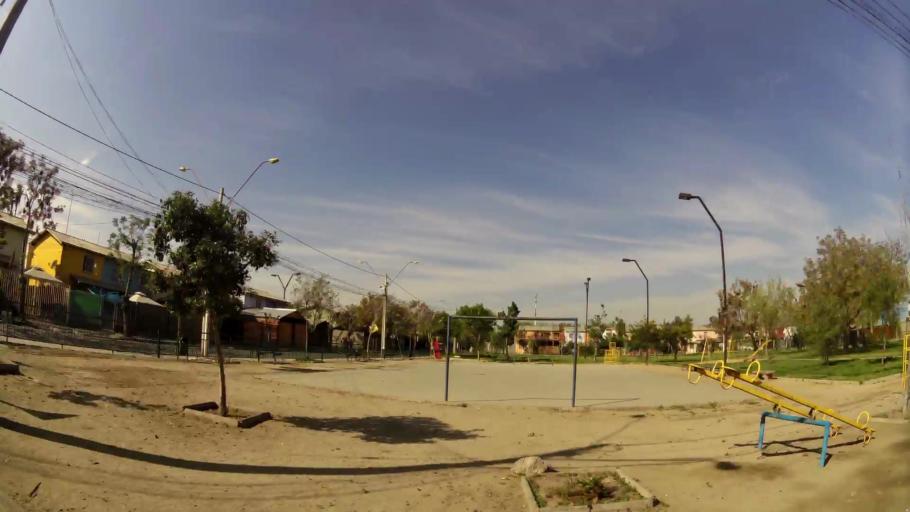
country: CL
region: Santiago Metropolitan
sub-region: Provincia de Santiago
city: La Pintana
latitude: -33.5638
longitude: -70.6336
